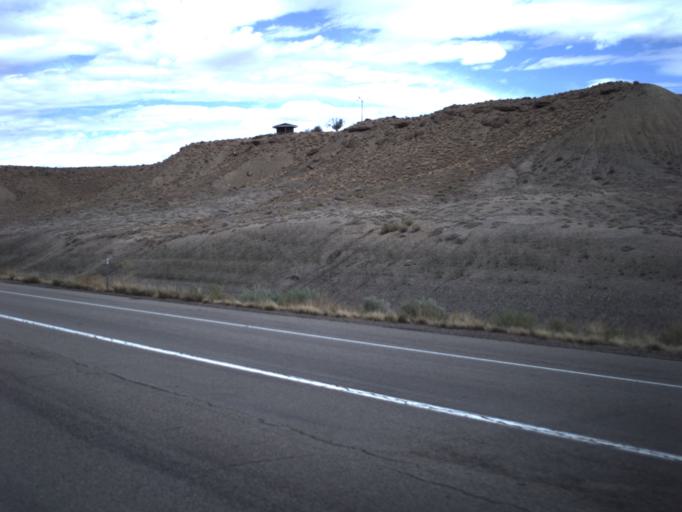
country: US
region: Utah
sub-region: Grand County
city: Moab
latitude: 38.9393
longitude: -109.8303
